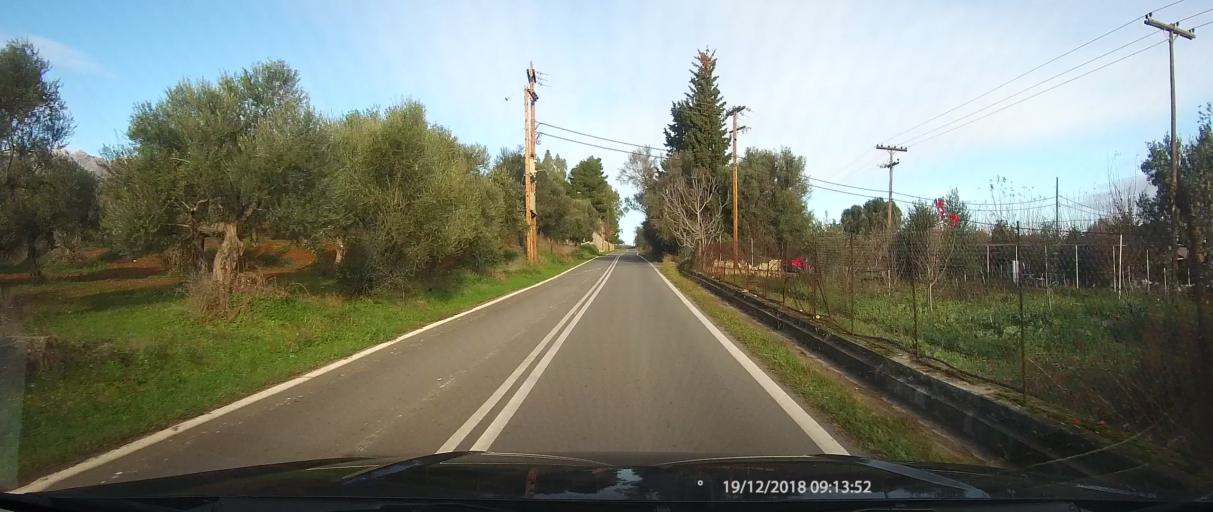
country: GR
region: Peloponnese
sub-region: Nomos Lakonias
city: Magoula
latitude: 37.0826
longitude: 22.3937
